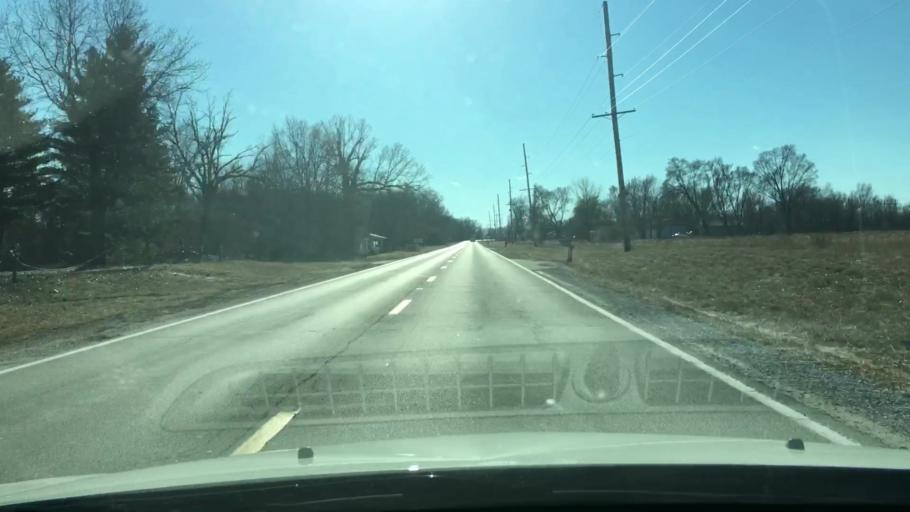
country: US
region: Illinois
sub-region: Cass County
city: Beardstown
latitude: 39.9487
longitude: -90.4855
